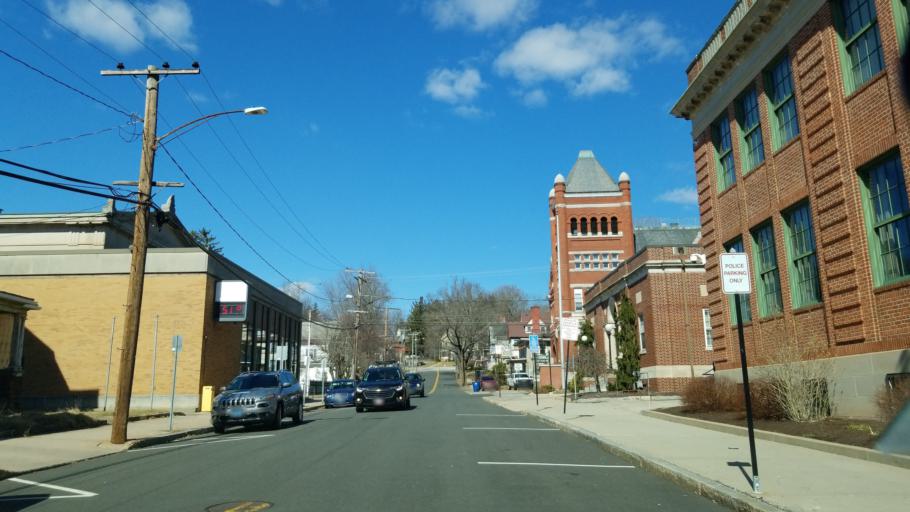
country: US
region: Connecticut
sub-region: Tolland County
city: Rockville
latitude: 41.8680
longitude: -72.4480
